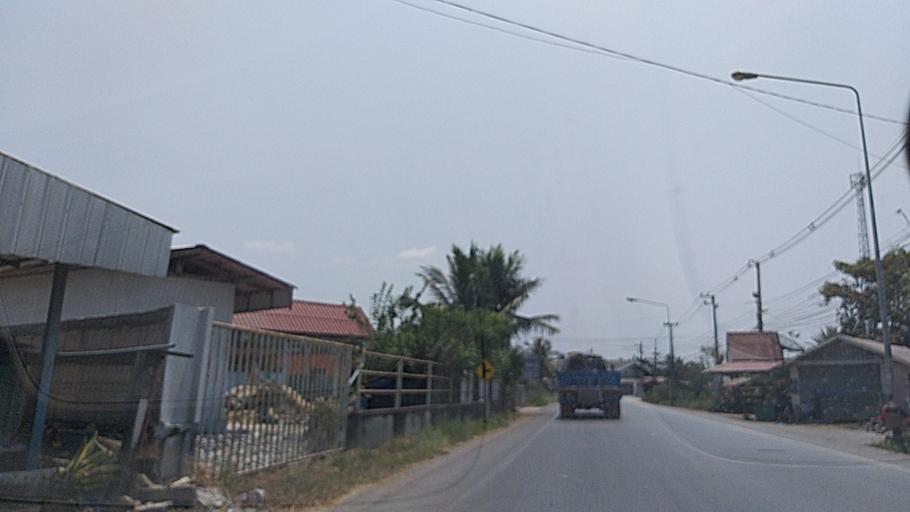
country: TH
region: Chachoengsao
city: Bang Nam Priao
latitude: 13.9426
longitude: 100.9783
